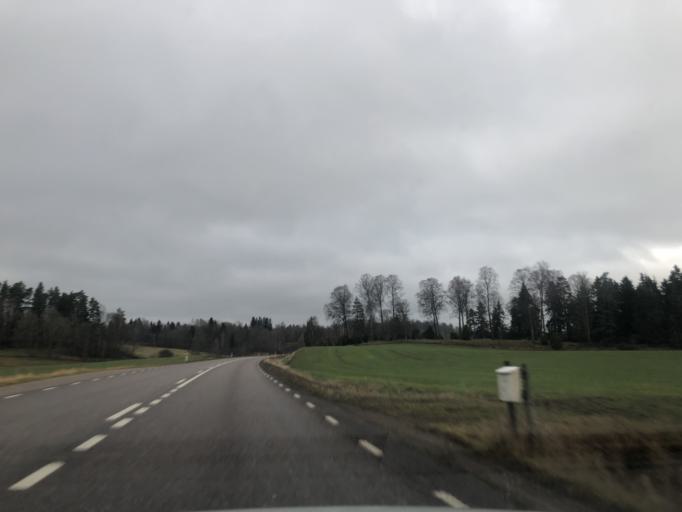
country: SE
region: Vaestra Goetaland
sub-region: Ulricehamns Kommun
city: Ulricehamn
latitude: 57.8802
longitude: 13.4335
